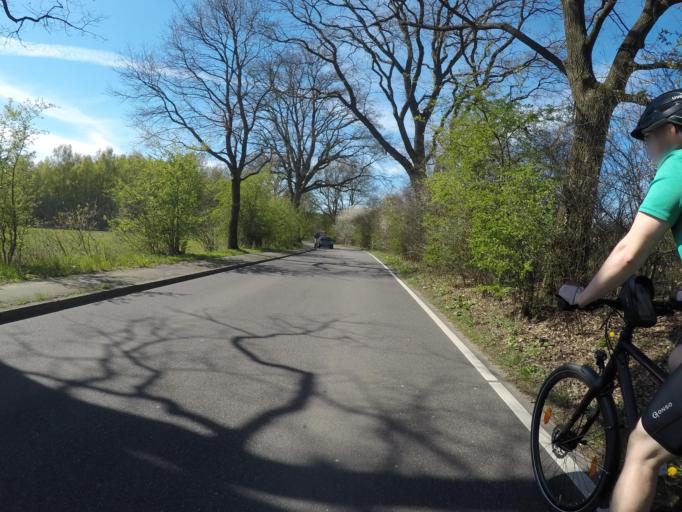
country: DE
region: Schleswig-Holstein
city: Tangstedt
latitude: 53.7133
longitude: 10.0798
